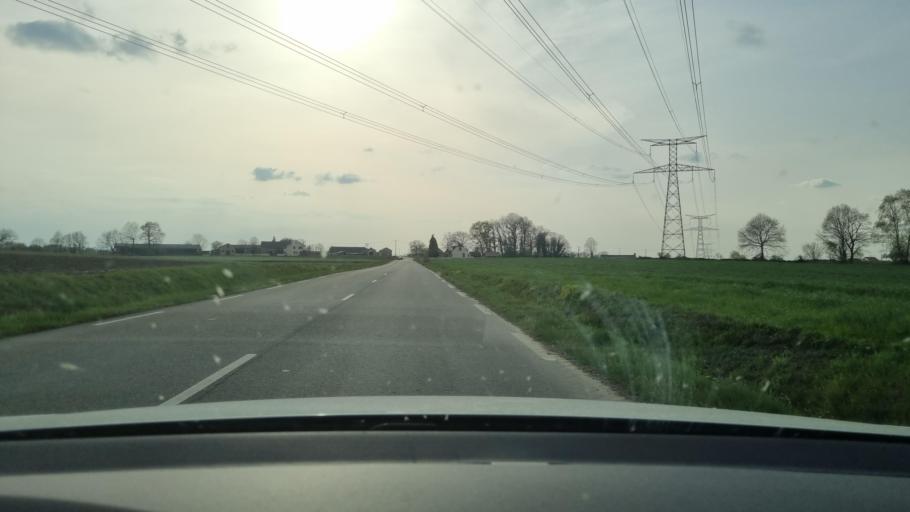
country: FR
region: Aquitaine
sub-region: Departement des Pyrenees-Atlantiques
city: Morlaas
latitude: 43.3734
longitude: -0.1682
